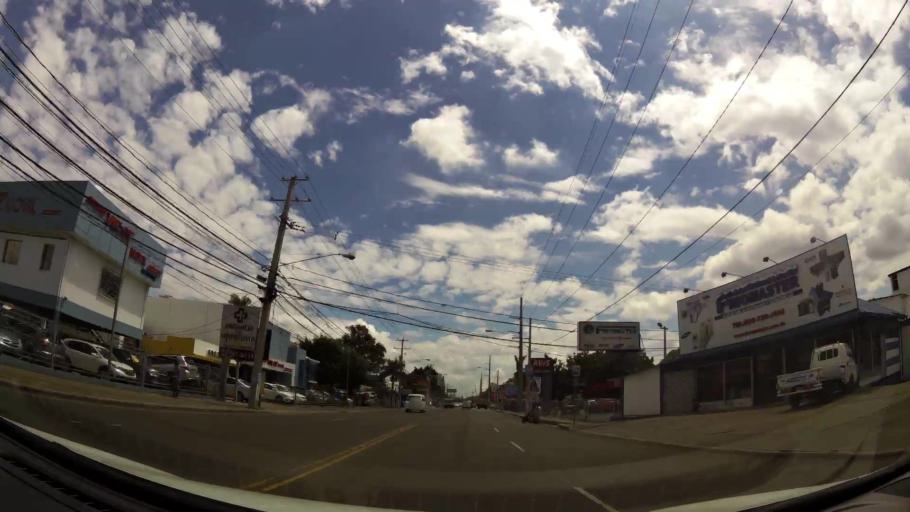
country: DO
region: Santiago
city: Santiago de los Caballeros
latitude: 19.4579
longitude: -70.6689
